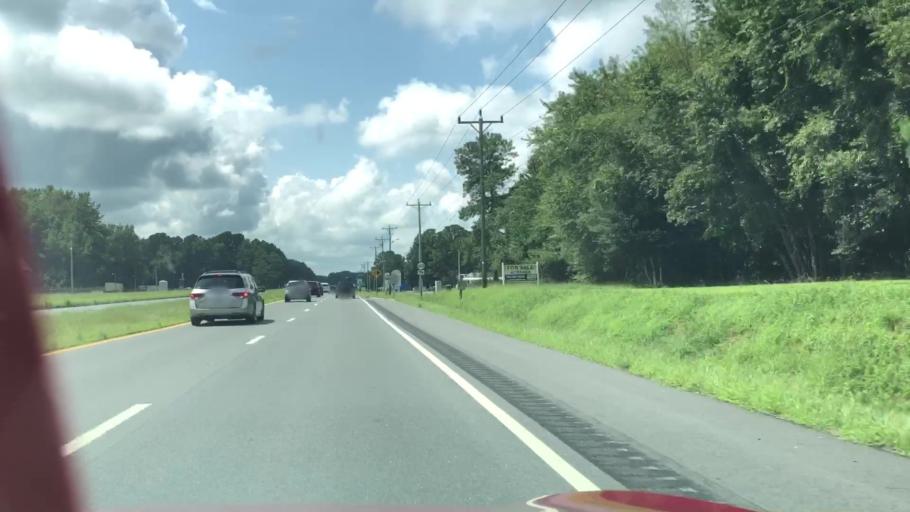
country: US
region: Virginia
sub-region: Northampton County
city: Exmore
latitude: 37.5524
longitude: -75.8073
